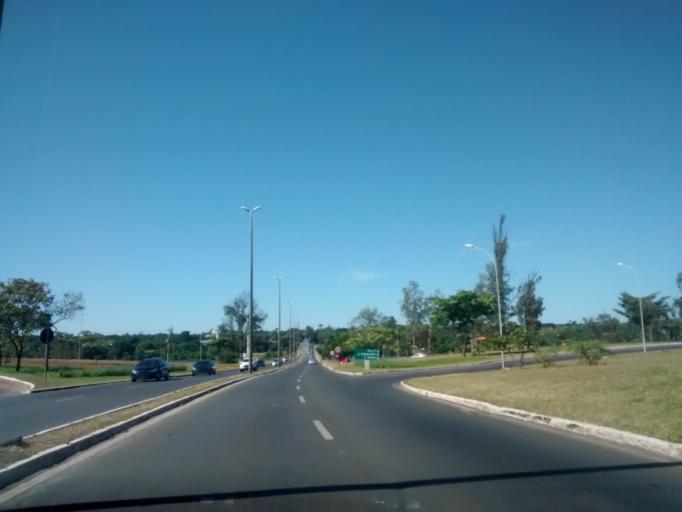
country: BR
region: Federal District
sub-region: Brasilia
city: Brasilia
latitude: -15.8361
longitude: -47.8997
